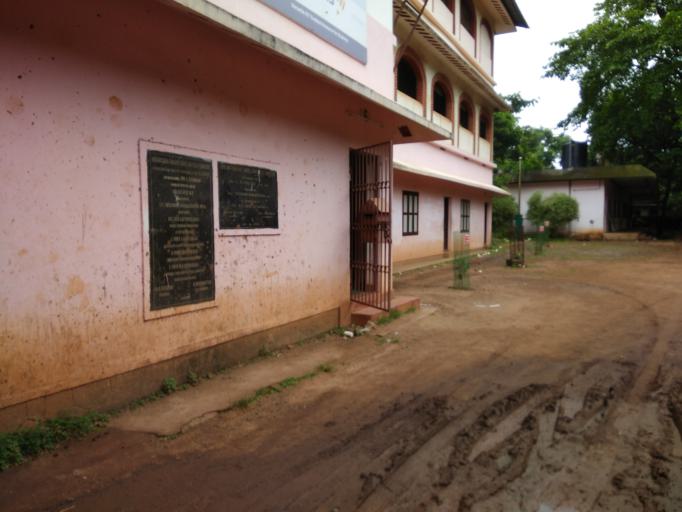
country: IN
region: Kerala
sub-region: Thrissur District
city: Trichur
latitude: 10.5274
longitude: 76.2193
